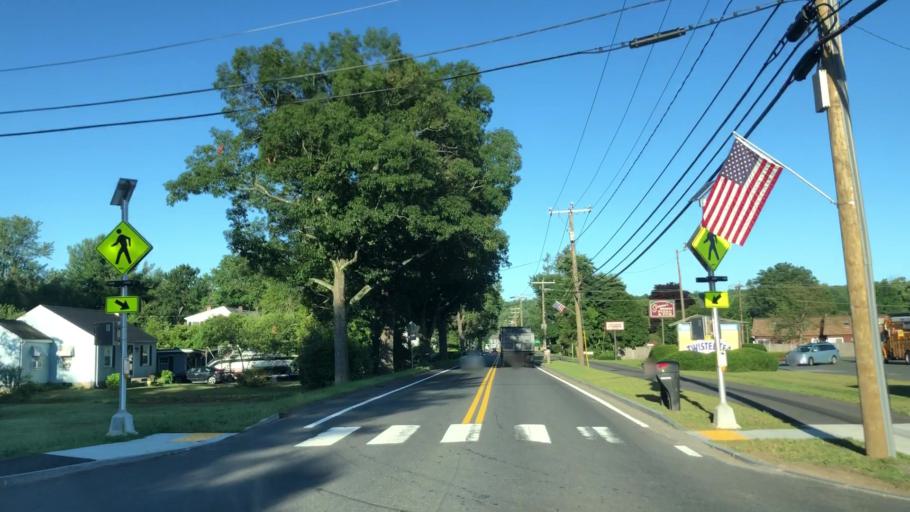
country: US
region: Massachusetts
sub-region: Hampshire County
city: Southampton
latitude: 42.2379
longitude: -72.7199
